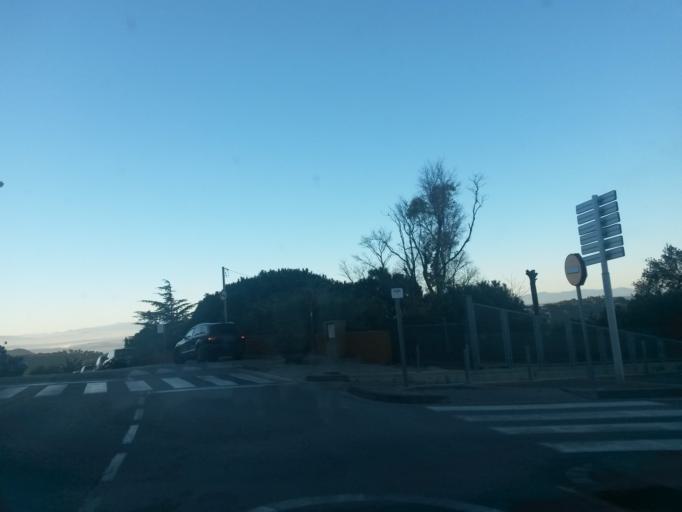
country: ES
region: Catalonia
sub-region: Provincia de Girona
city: Begur
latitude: 41.9526
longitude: 3.2064
